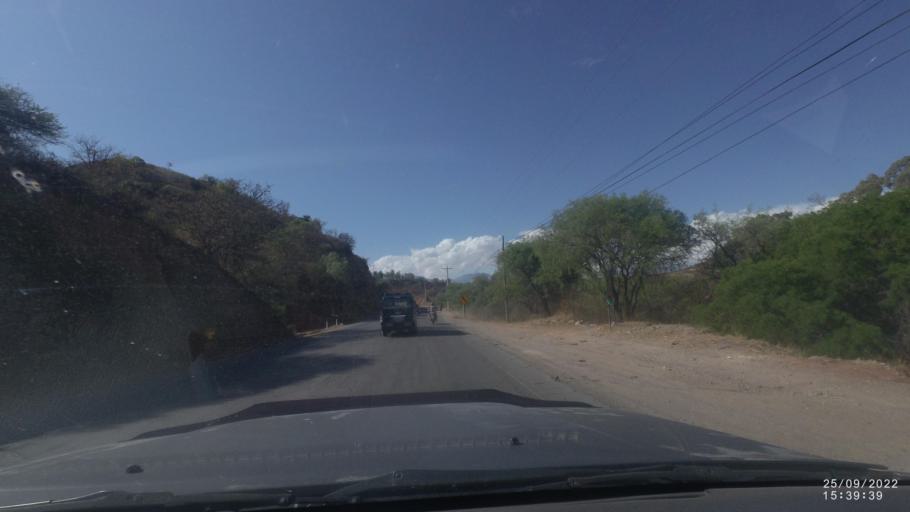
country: BO
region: Cochabamba
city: Sipe Sipe
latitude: -17.4842
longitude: -66.3387
